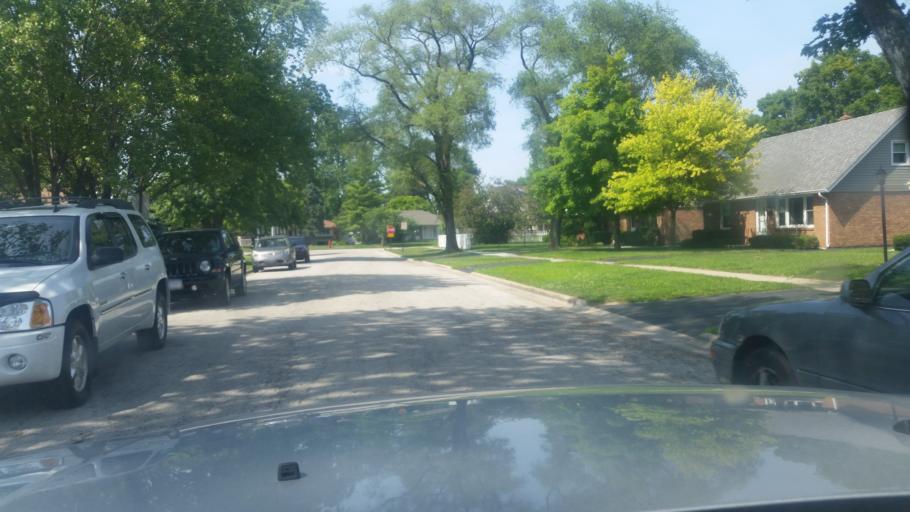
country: US
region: Illinois
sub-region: Cook County
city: Chicago Ridge
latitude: 41.6916
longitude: -87.7666
